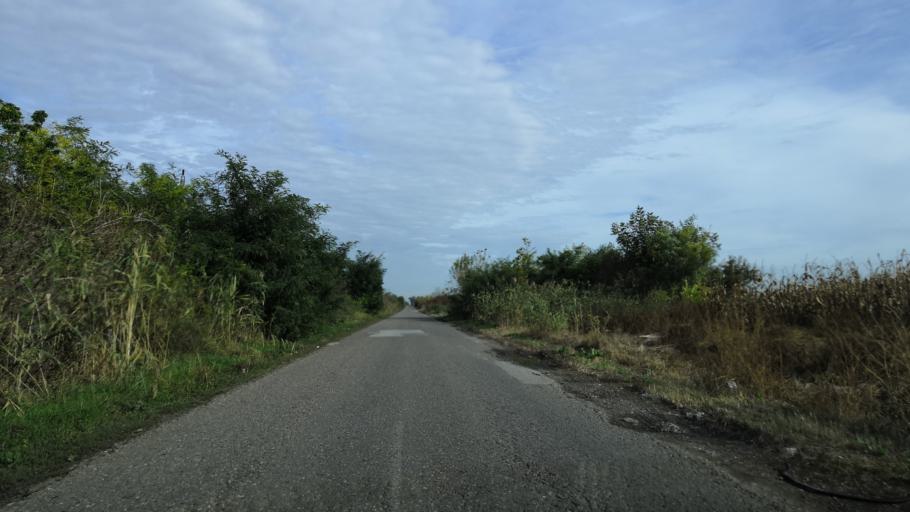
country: RS
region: Autonomna Pokrajina Vojvodina
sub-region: Sremski Okrug
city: Stara Pazova
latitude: 44.9981
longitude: 20.1644
